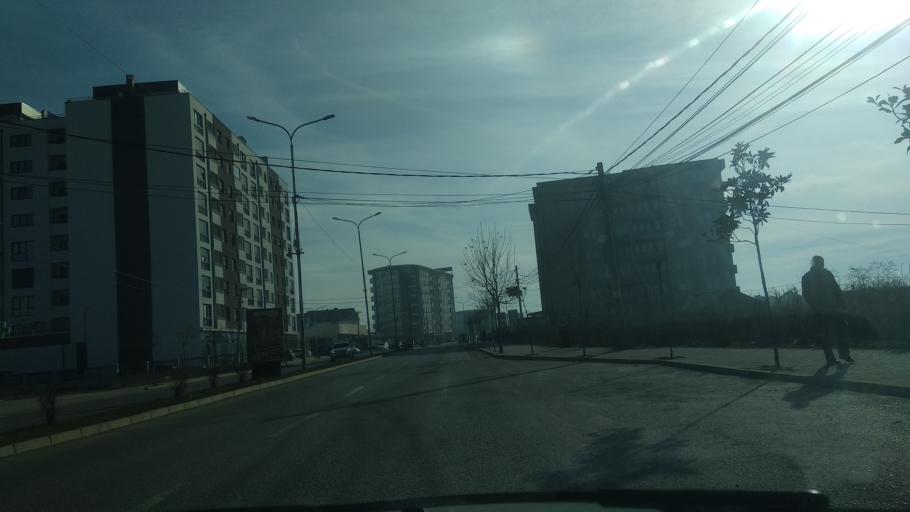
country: XK
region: Mitrovica
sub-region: Vushtrri
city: Vushtrri
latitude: 42.8188
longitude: 20.9786
